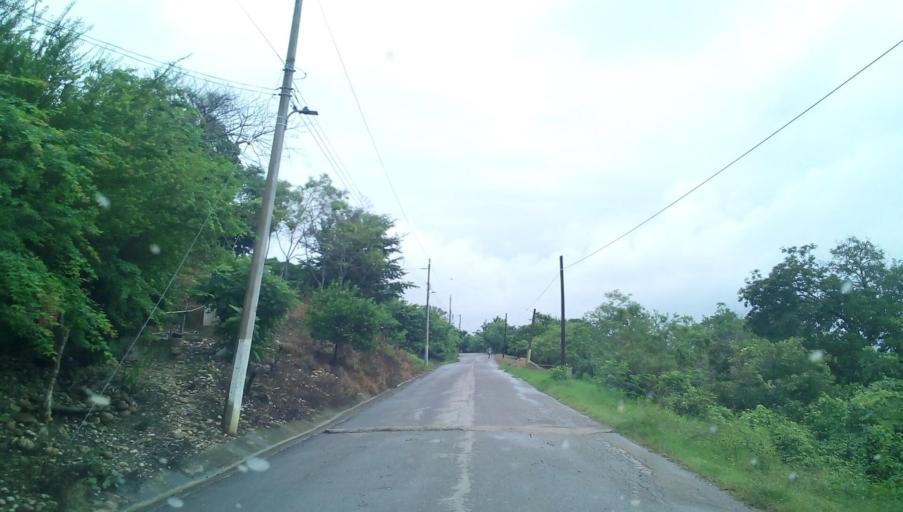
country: MX
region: Veracruz
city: Tempoal de Sanchez
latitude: 21.4627
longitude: -98.4230
